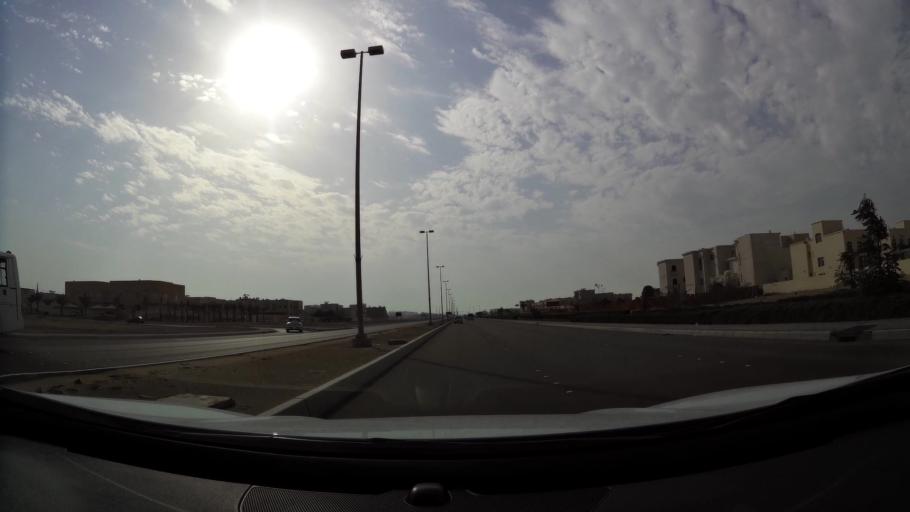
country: AE
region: Abu Dhabi
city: Abu Dhabi
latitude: 24.3481
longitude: 54.5590
